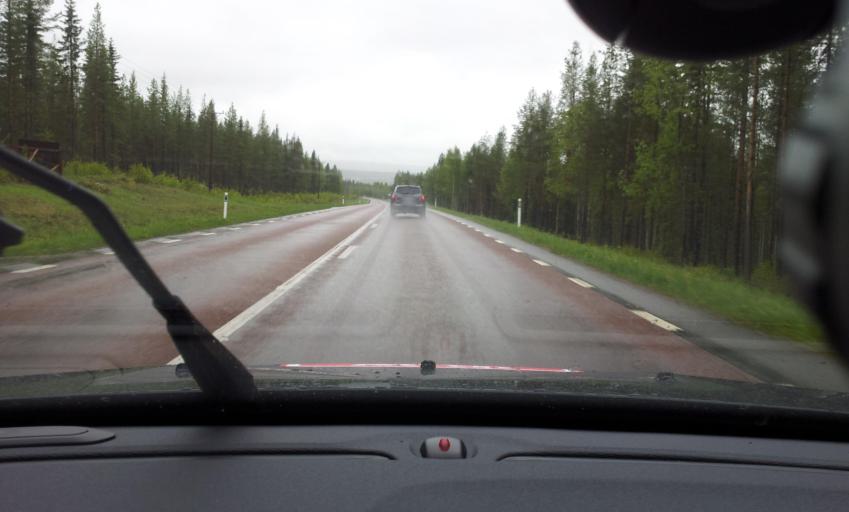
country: SE
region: Jaemtland
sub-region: Bergs Kommun
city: Hoverberg
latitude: 62.7896
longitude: 14.4685
